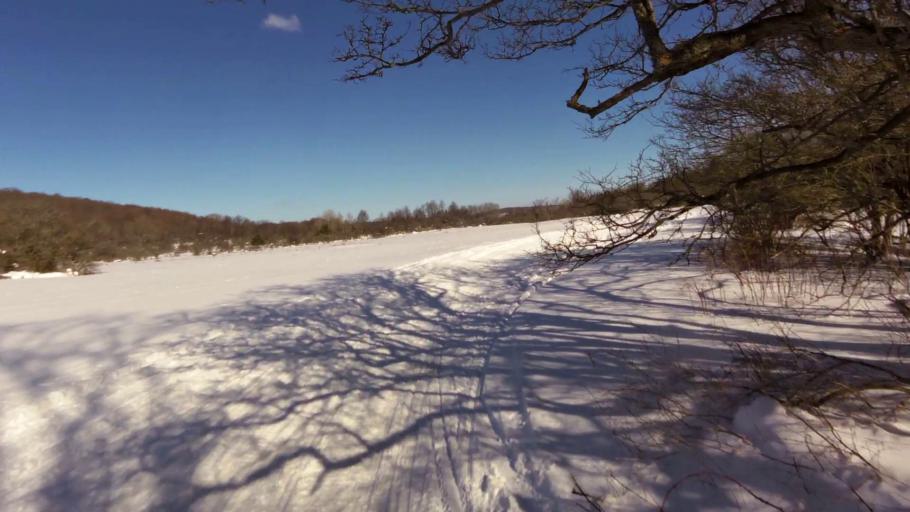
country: US
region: New York
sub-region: Cattaraugus County
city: Franklinville
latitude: 42.3974
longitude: -78.4950
